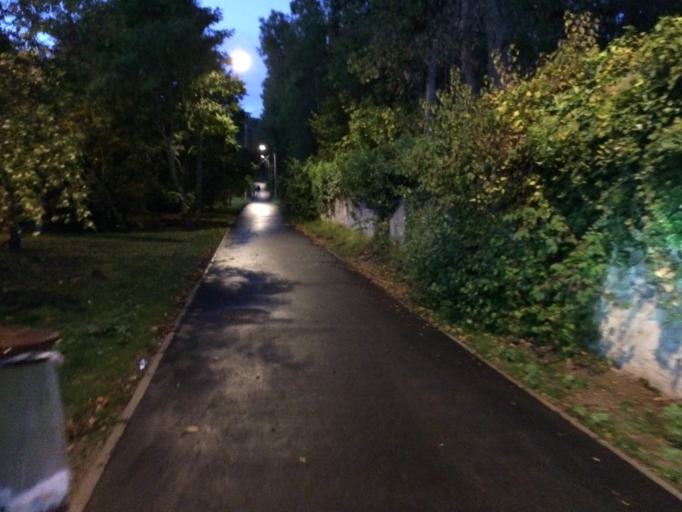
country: FR
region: Ile-de-France
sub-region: Departement de l'Essonne
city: Bures-sur-Yvette
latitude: 48.7016
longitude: 2.1649
